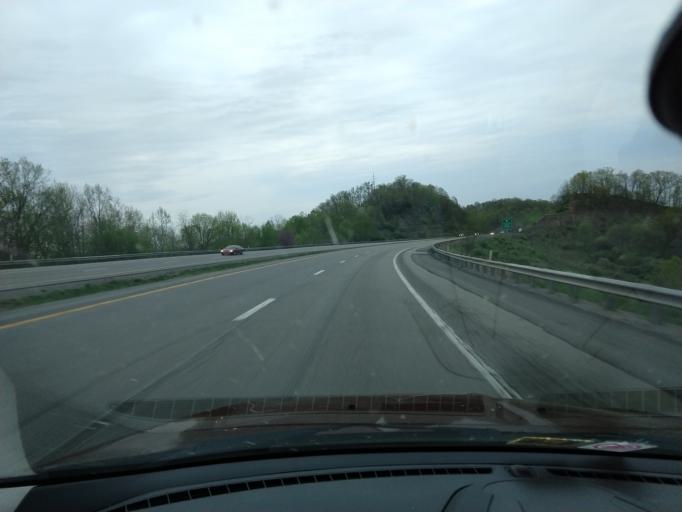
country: US
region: West Virginia
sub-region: Lewis County
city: Weston
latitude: 38.9433
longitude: -80.5409
